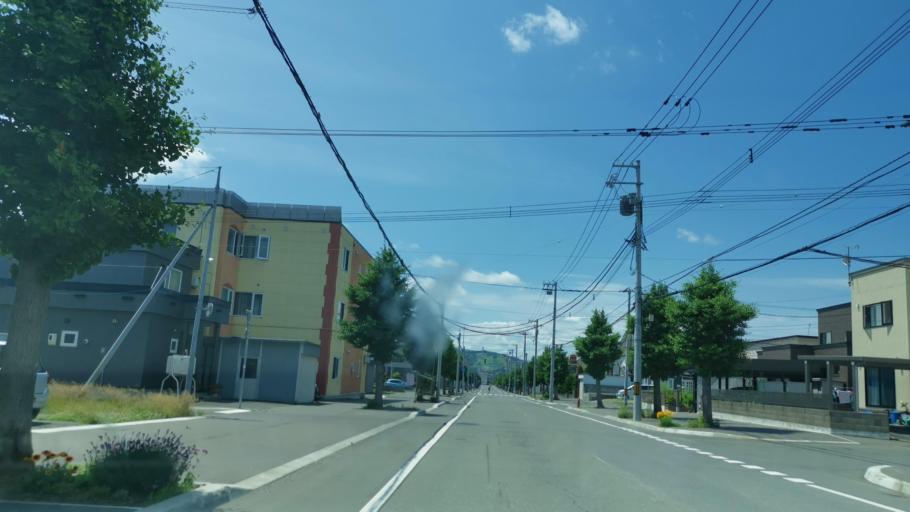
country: JP
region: Hokkaido
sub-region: Asahikawa-shi
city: Asahikawa
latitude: 43.7913
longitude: 142.3451
